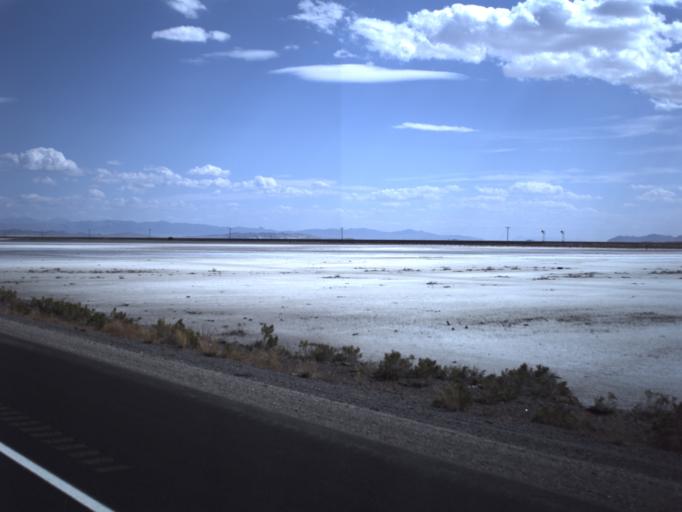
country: US
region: Utah
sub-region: Tooele County
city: Wendover
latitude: 40.7309
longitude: -113.5015
